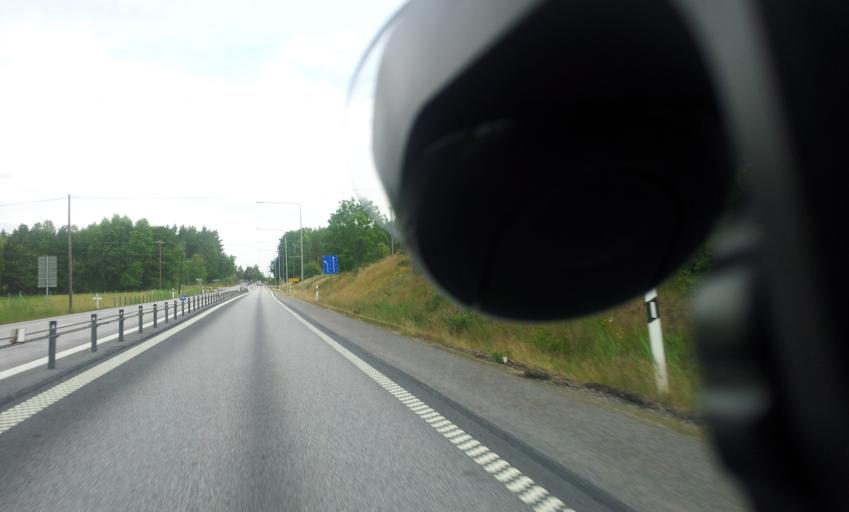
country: SE
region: OEstergoetland
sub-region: Soderkopings Kommun
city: Soederkoeping
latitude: 58.4385
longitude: 16.3753
